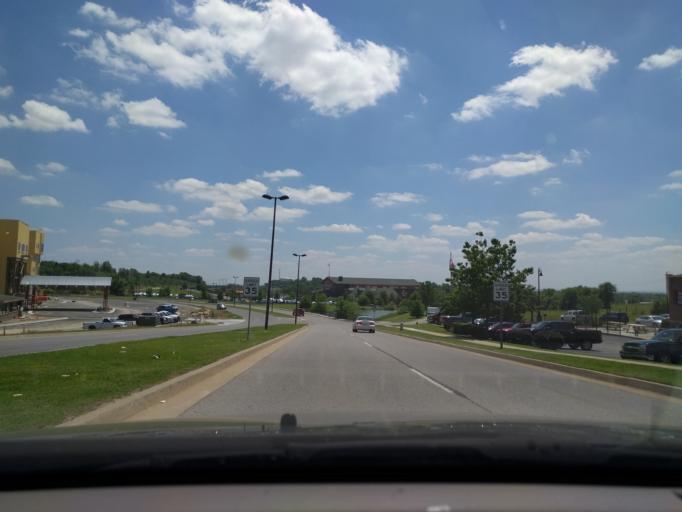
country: US
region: Oklahoma
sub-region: Tulsa County
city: Broken Arrow
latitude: 36.0740
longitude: -95.7944
